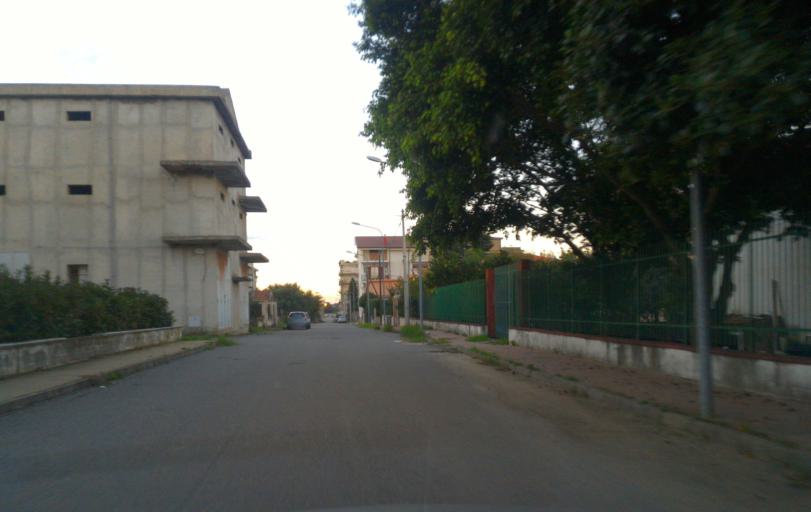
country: IT
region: Calabria
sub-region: Provincia di Crotone
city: Torretta
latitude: 39.4538
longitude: 17.0349
